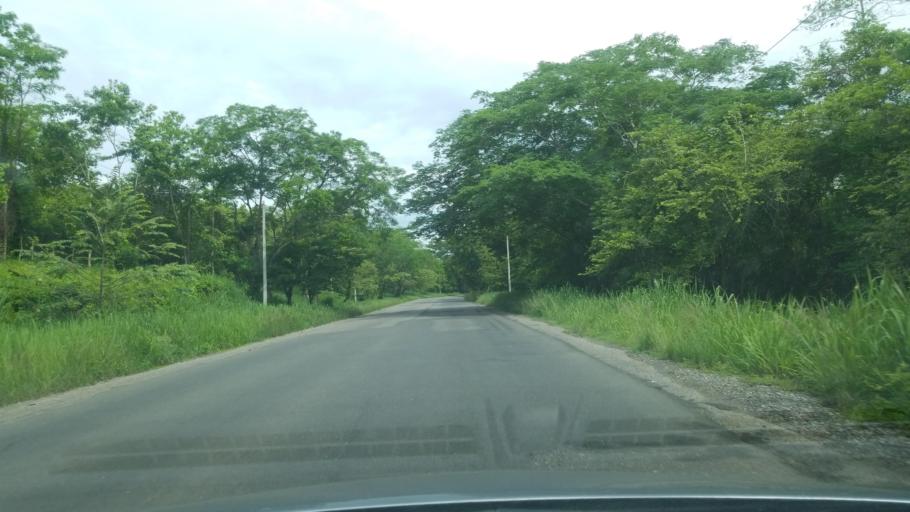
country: HN
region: Santa Barbara
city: Camalote
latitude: 15.3352
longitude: -88.3516
